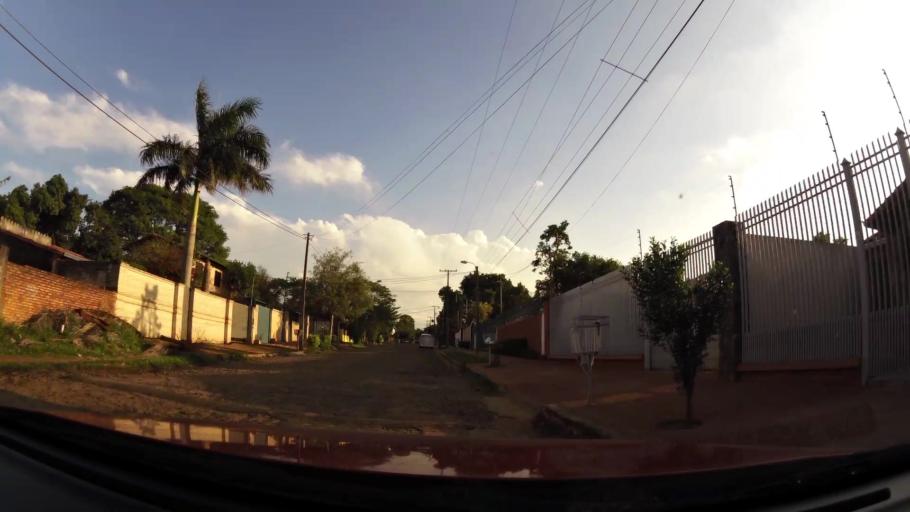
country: PY
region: Central
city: San Lorenzo
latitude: -25.3569
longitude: -57.5160
